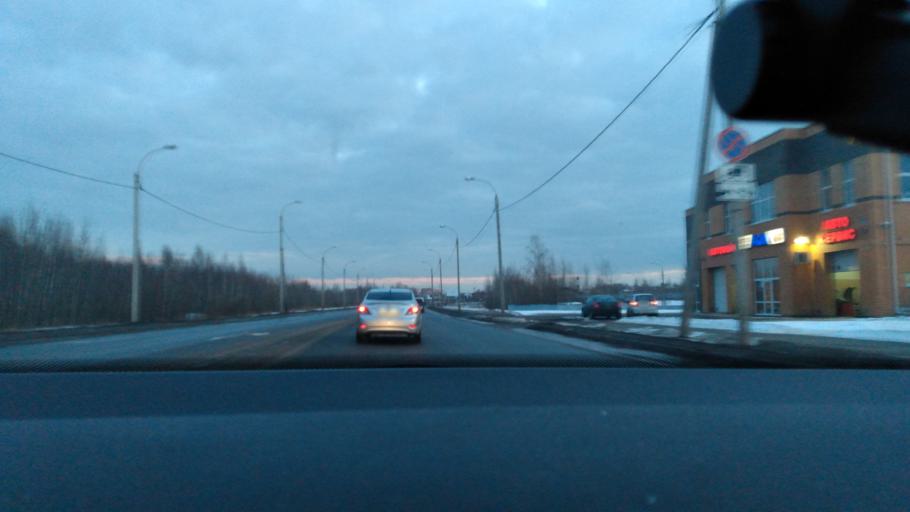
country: RU
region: Moskovskaya
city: Yegor'yevsk
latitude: 55.3831
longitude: 39.0655
